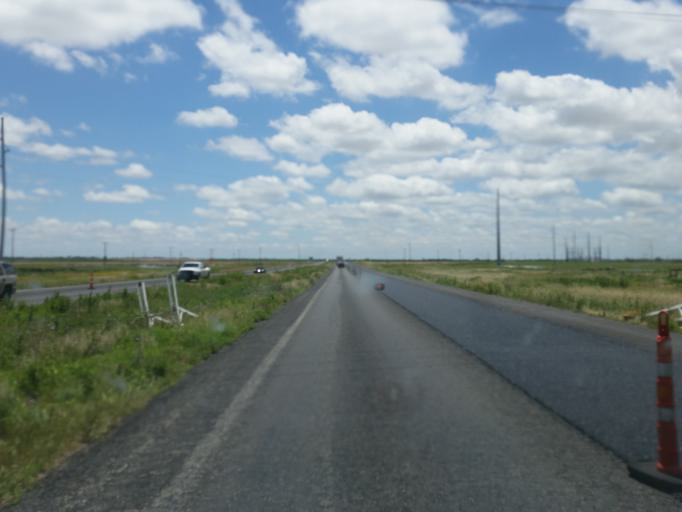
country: US
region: Texas
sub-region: Scurry County
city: Snyder
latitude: 32.7833
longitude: -100.9467
